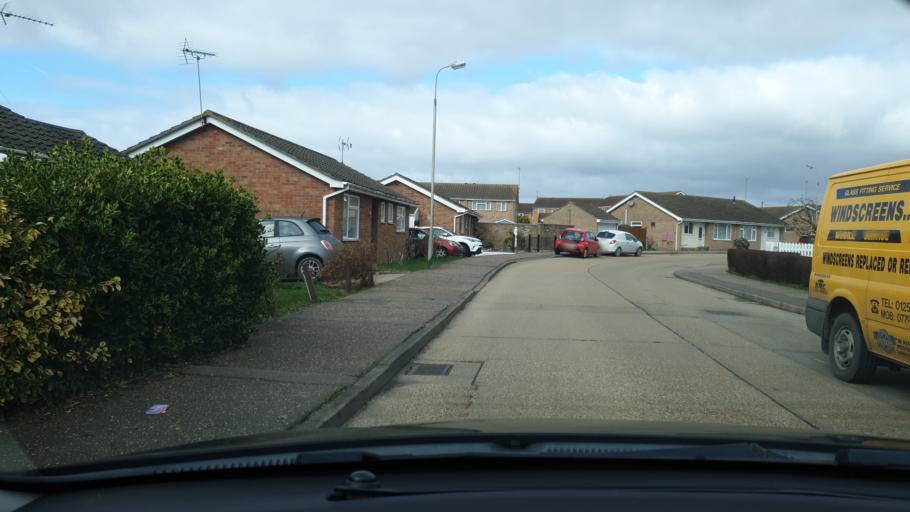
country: GB
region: England
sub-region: Essex
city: Little Clacton
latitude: 51.8136
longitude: 1.1557
